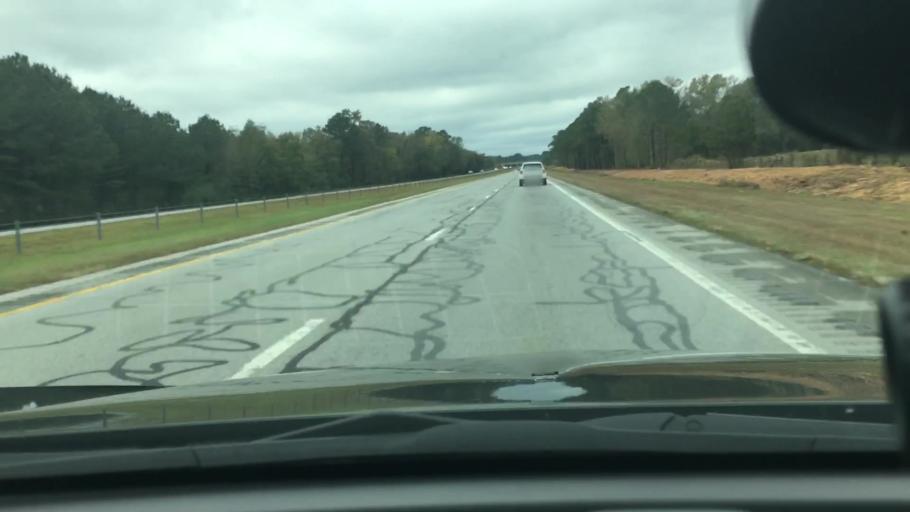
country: US
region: North Carolina
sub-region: Pitt County
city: Farmville
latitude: 35.6157
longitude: -77.6297
